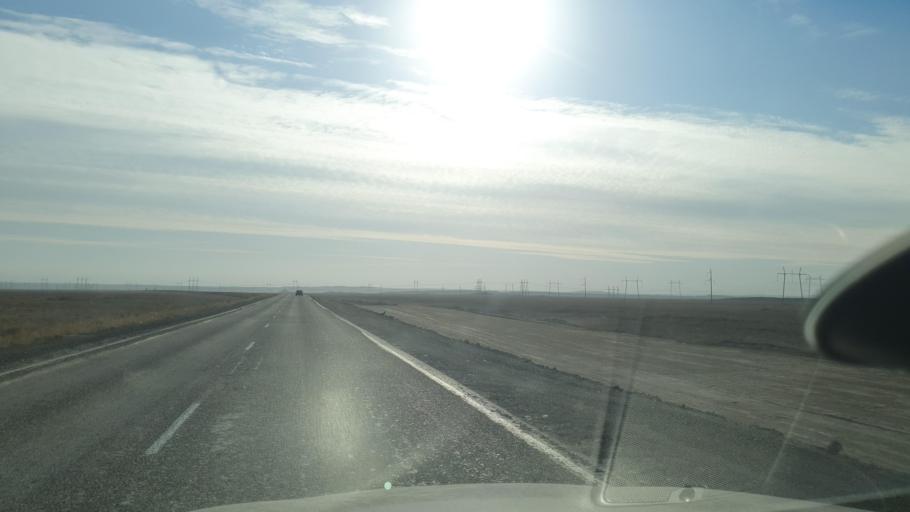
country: KZ
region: Zhambyl
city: Mynaral
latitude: 45.6176
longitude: 73.3959
